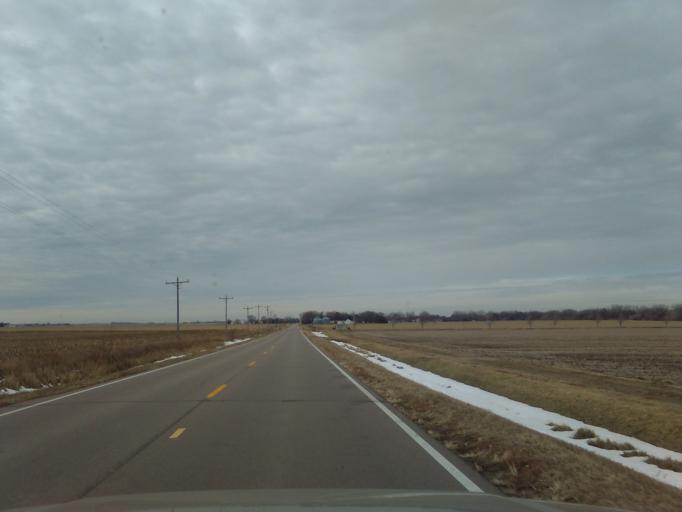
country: US
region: Nebraska
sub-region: Hall County
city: Grand Island
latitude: 40.7709
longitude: -98.3990
